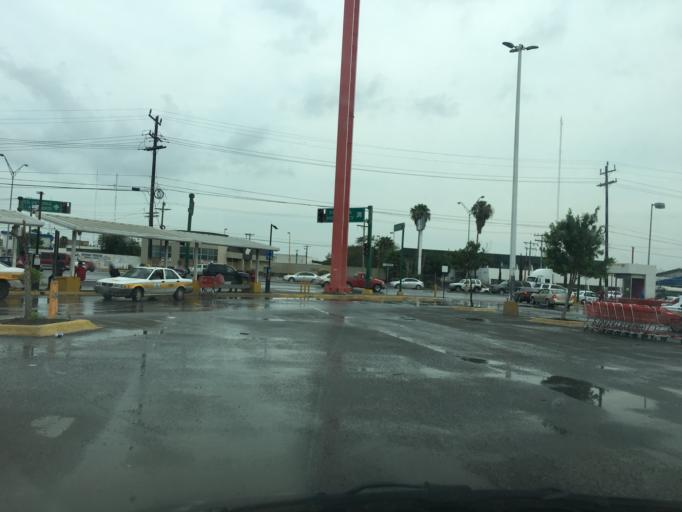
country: MX
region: Tamaulipas
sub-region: Matamoros
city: Heroica Matamoros
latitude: 25.8772
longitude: -97.5215
